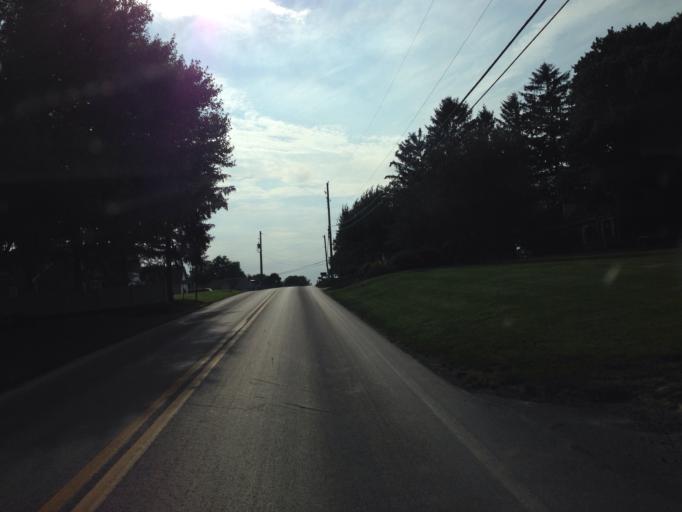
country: US
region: Pennsylvania
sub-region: Lancaster County
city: Lampeter
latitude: 40.0514
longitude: -76.2051
